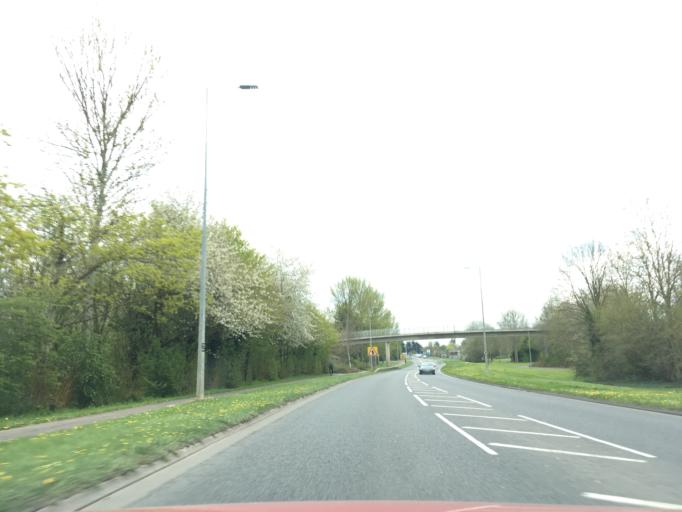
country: GB
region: England
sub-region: Milton Keynes
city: Newport Pagnell
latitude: 52.0590
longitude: -0.7293
